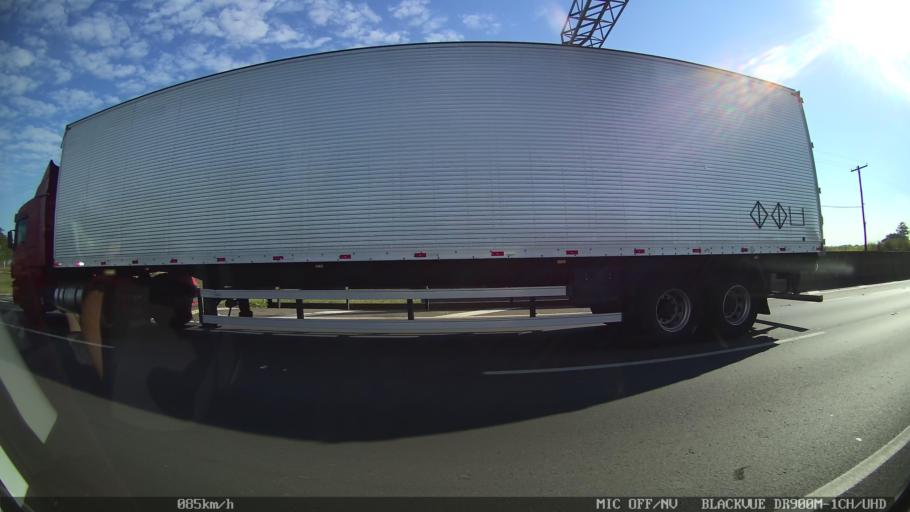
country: BR
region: Sao Paulo
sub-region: Sumare
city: Sumare
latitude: -22.7771
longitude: -47.2342
